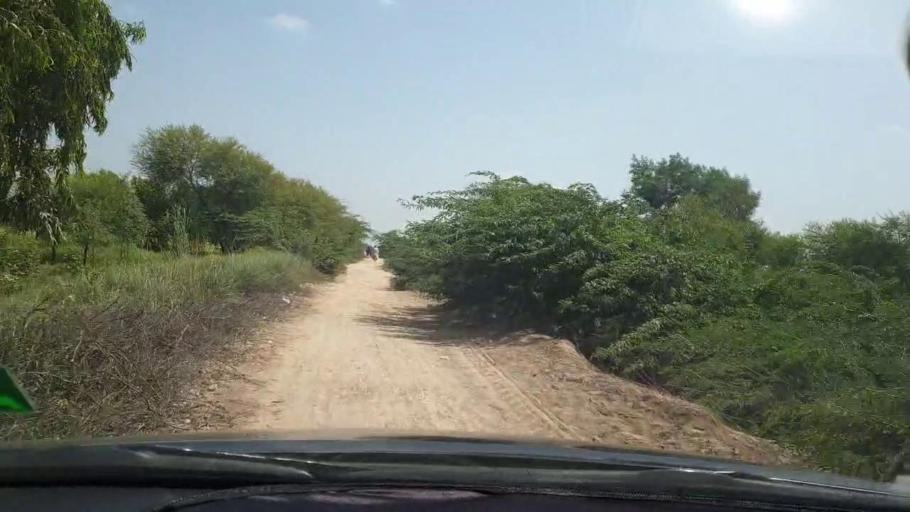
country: PK
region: Sindh
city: Tando Bago
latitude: 24.8958
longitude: 69.0859
